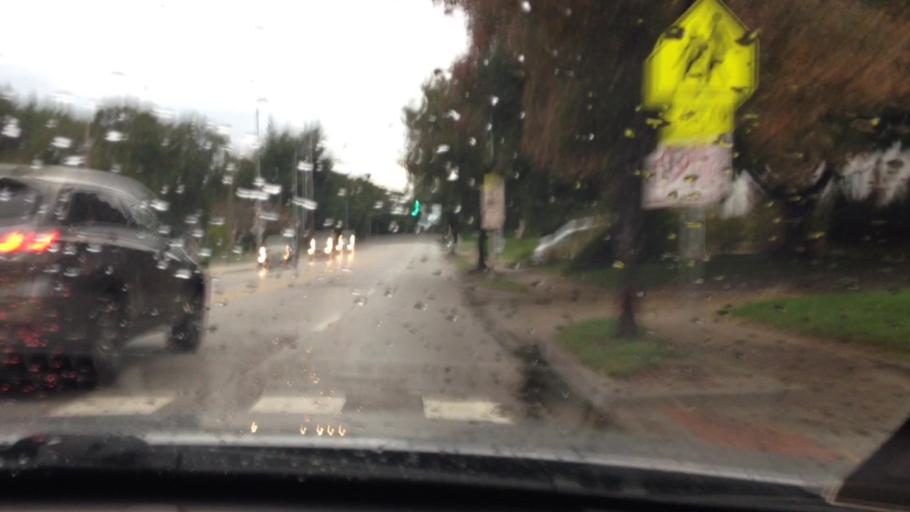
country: US
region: Kansas
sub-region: Johnson County
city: Mission Hills
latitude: 39.0113
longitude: -94.5932
